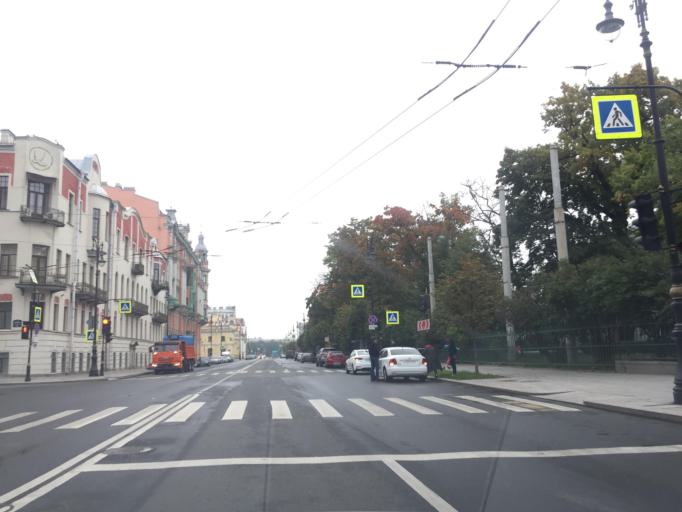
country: RU
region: St.-Petersburg
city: Centralniy
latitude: 59.9462
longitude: 30.3675
